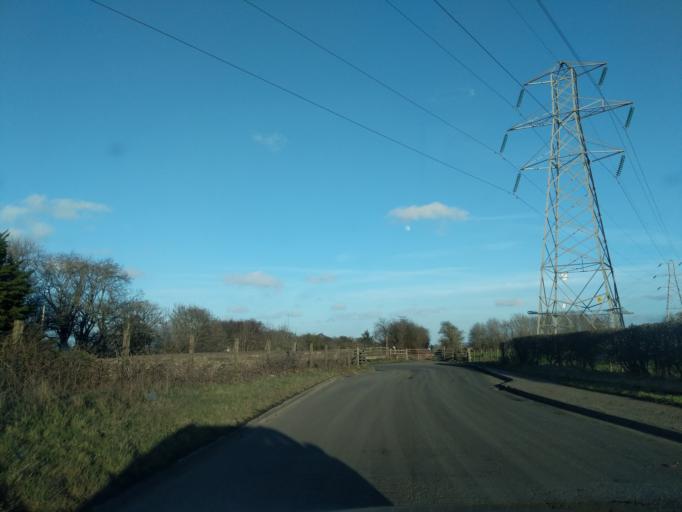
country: GB
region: Scotland
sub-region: Edinburgh
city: Ratho
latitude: 55.8926
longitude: -3.3839
